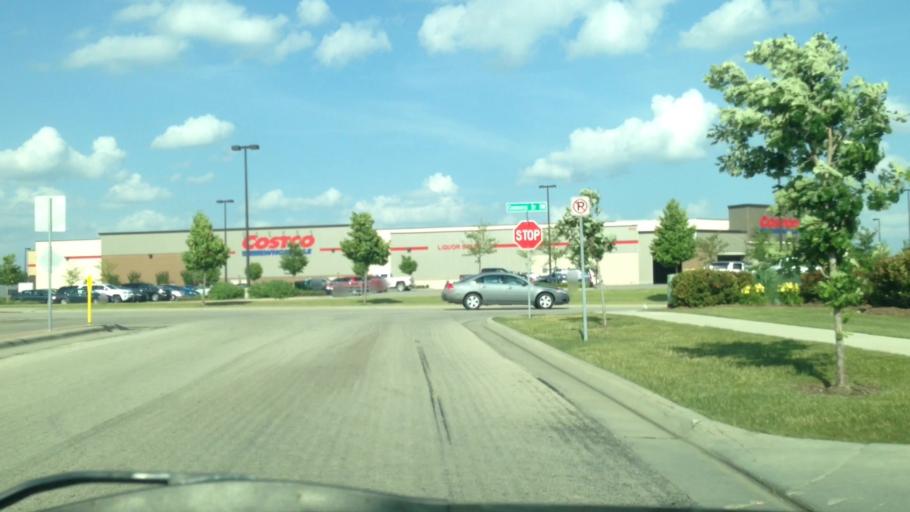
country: US
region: Minnesota
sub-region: Olmsted County
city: Rochester
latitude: 44.0469
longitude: -92.5194
